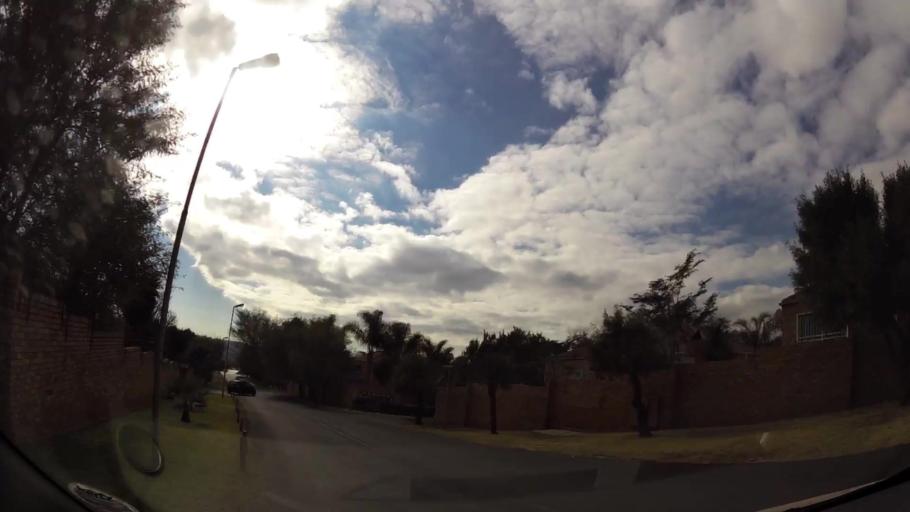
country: ZA
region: Gauteng
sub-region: City of Johannesburg Metropolitan Municipality
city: Roodepoort
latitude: -26.0990
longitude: 27.8700
